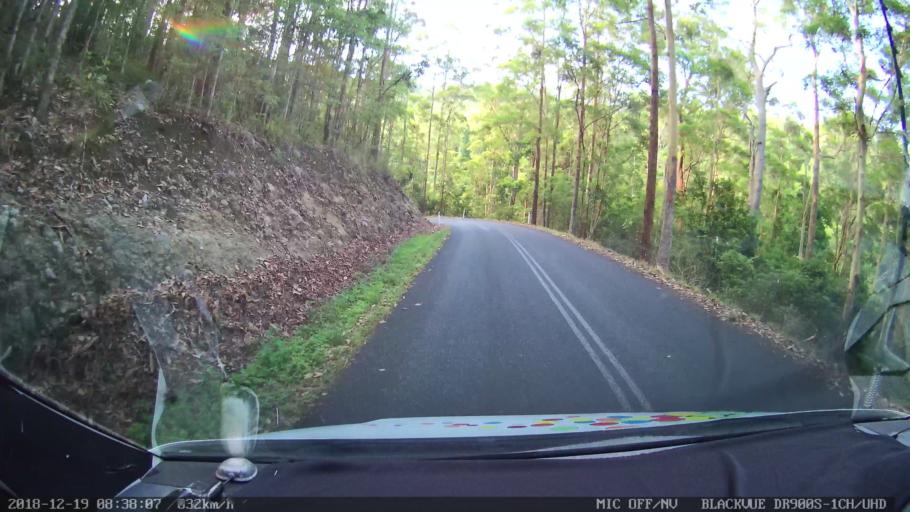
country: AU
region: New South Wales
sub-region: Kyogle
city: Kyogle
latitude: -28.3339
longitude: 152.9744
